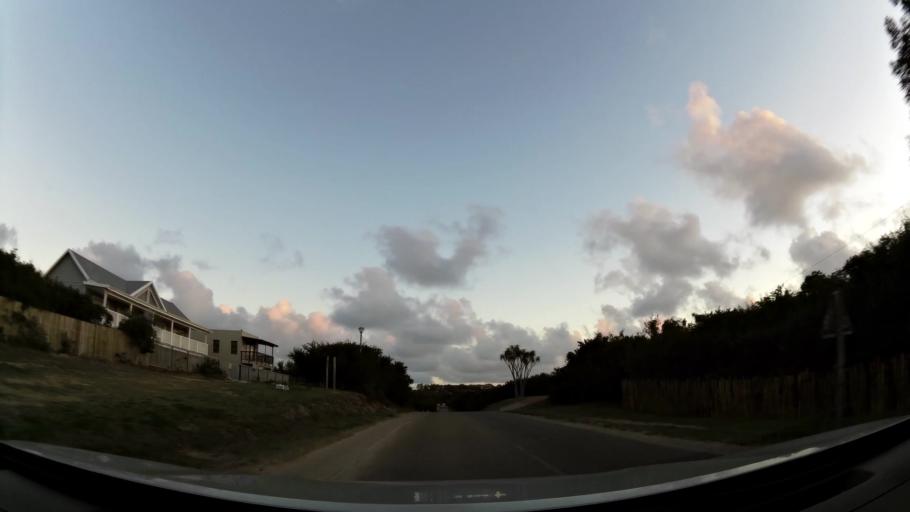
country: ZA
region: Western Cape
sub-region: Eden District Municipality
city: Knysna
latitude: -34.0252
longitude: 22.8077
